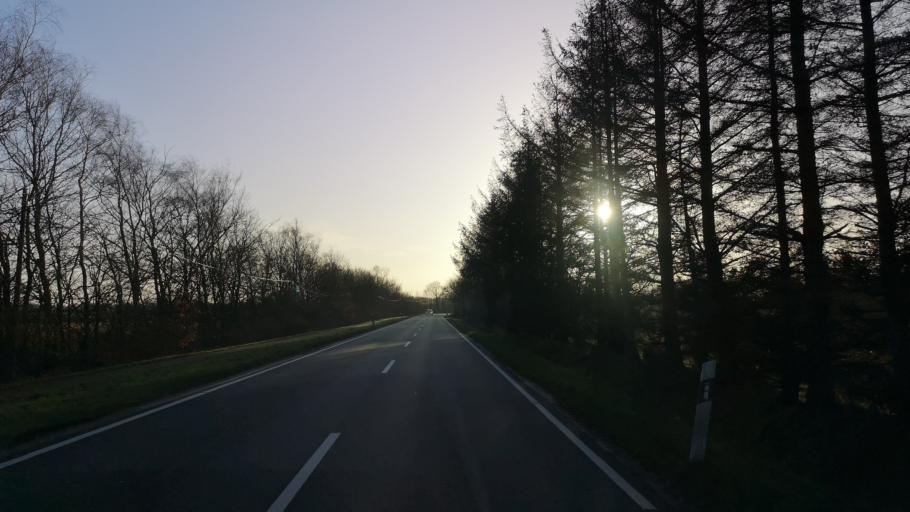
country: DE
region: Schleswig-Holstein
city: Sieverstedt
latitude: 54.6708
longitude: 9.4799
